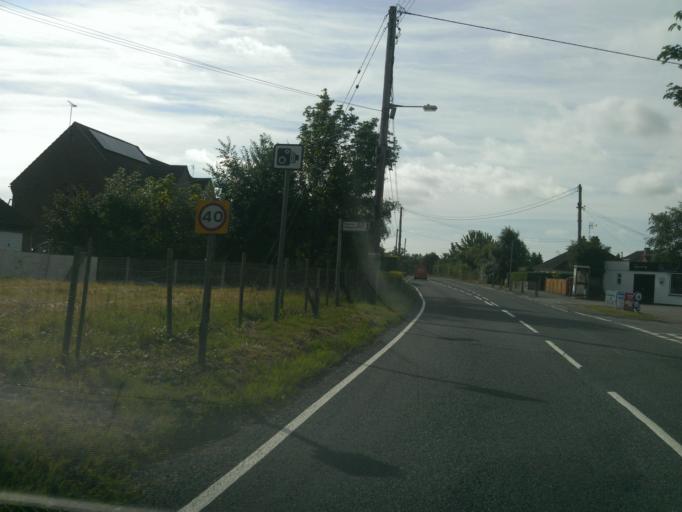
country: GB
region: England
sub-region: Essex
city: Alresford
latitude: 51.8580
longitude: 0.9990
